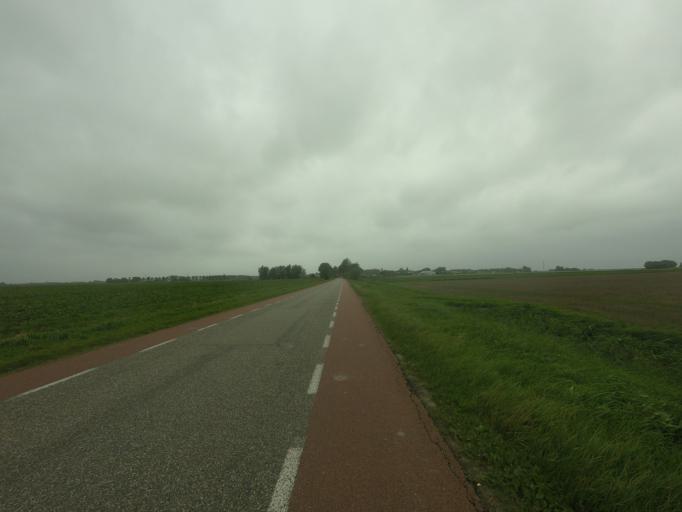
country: NL
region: Friesland
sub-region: Gemeente Ferwerderadiel
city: Ferwert
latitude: 53.3353
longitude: 5.8442
